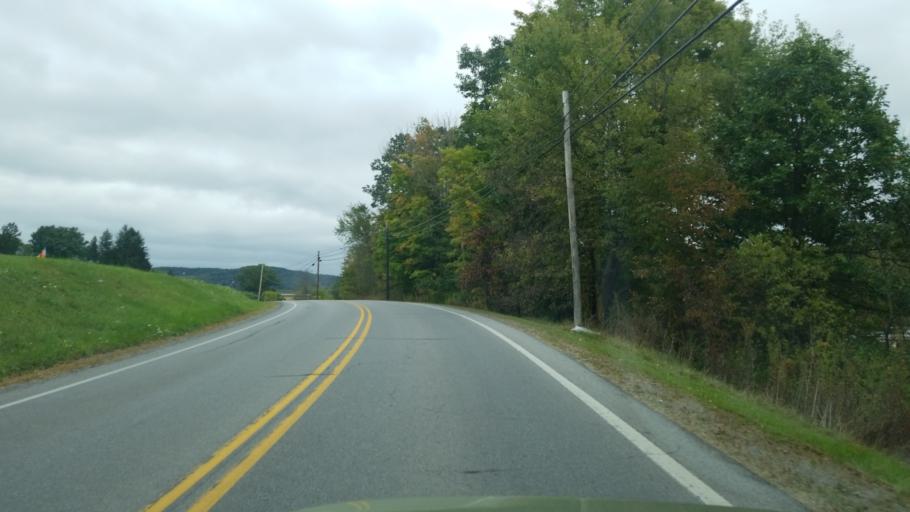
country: US
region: Pennsylvania
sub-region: Clearfield County
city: Hyde
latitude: 40.9937
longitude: -78.4678
